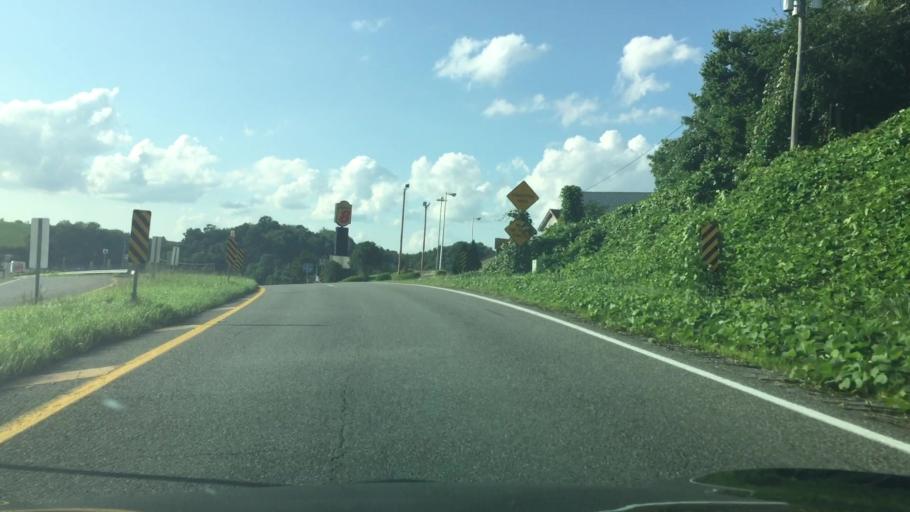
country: US
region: Virginia
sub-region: Wythe County
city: Wytheville
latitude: 36.9422
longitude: -80.9447
